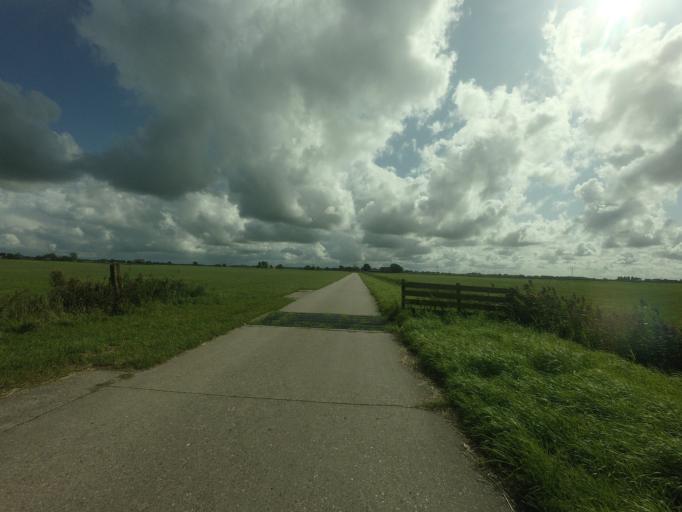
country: NL
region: Friesland
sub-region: Sudwest Fryslan
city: Scharnegoutum
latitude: 53.0689
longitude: 5.6387
